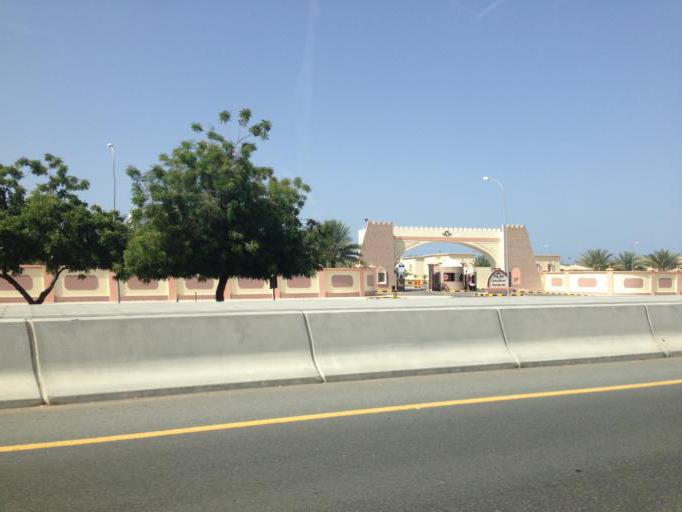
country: OM
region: Muhafazat Masqat
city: Bawshar
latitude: 23.6037
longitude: 58.3344
